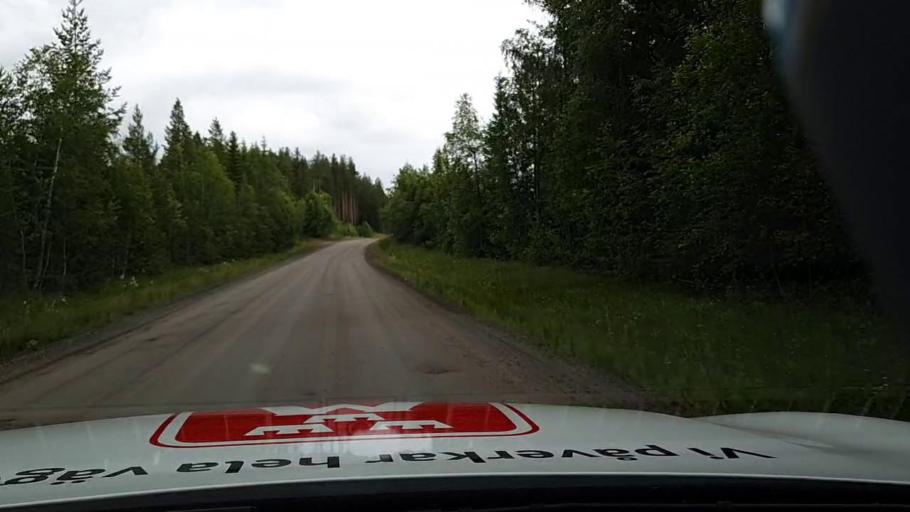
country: SE
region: Vaesternorrland
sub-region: Solleftea Kommun
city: As
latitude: 63.5106
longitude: 16.4043
